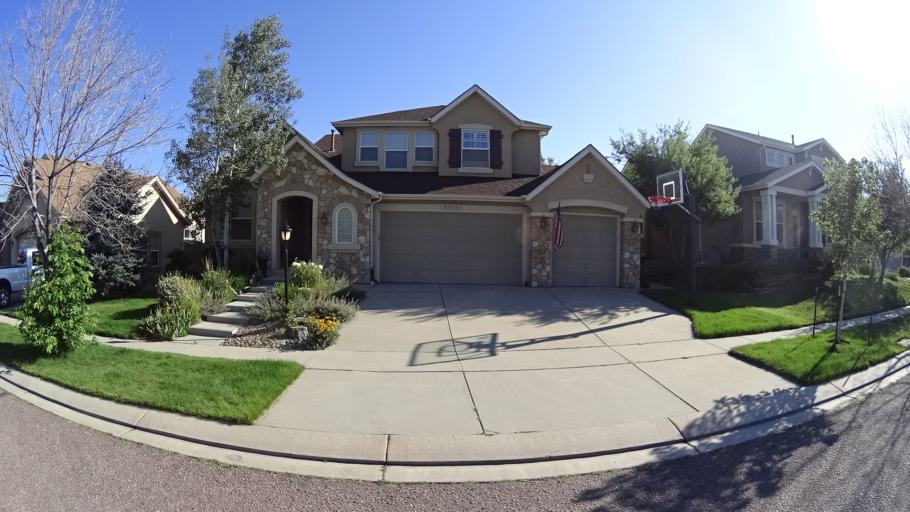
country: US
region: Colorado
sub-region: El Paso County
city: Black Forest
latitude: 38.9816
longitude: -104.7634
